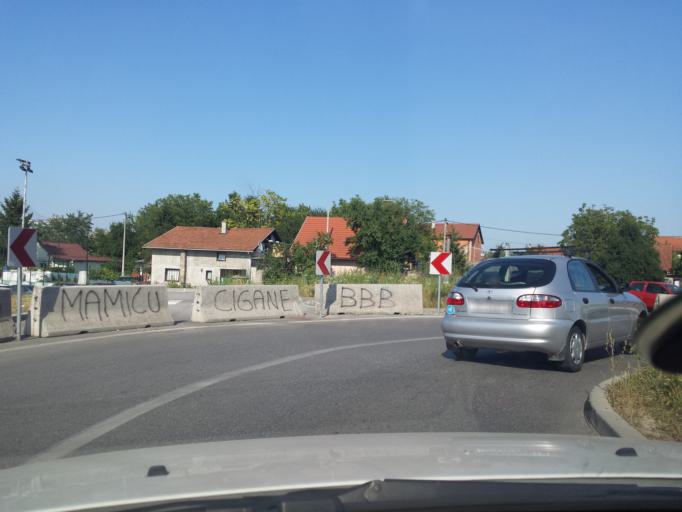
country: HR
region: Grad Zagreb
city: Jankomir
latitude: 45.8019
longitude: 15.9069
